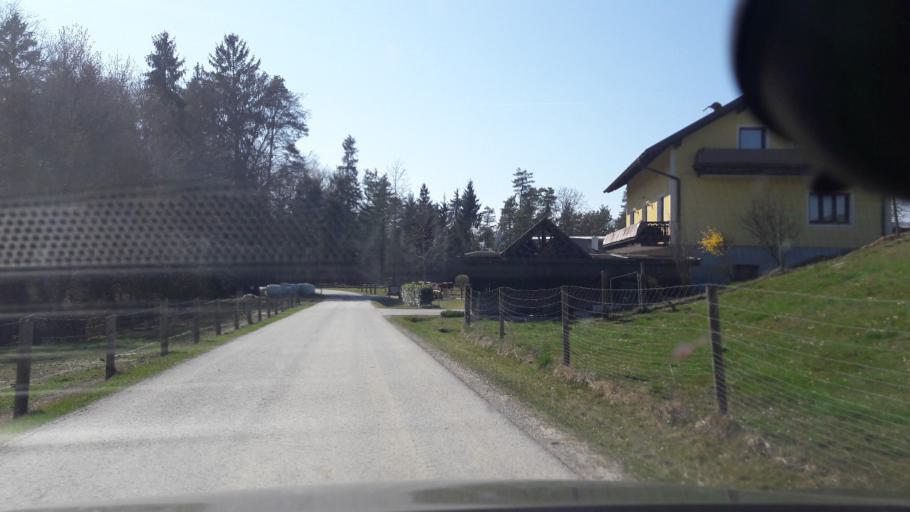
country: AT
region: Styria
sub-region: Politischer Bezirk Graz-Umgebung
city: Hitzendorf
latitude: 47.0395
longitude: 15.3201
